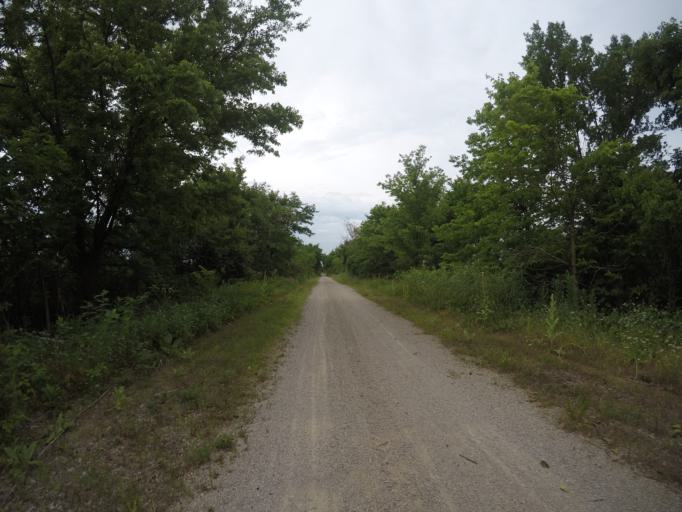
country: US
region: Kansas
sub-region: Franklin County
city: Ottawa
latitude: 38.5230
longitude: -95.2723
